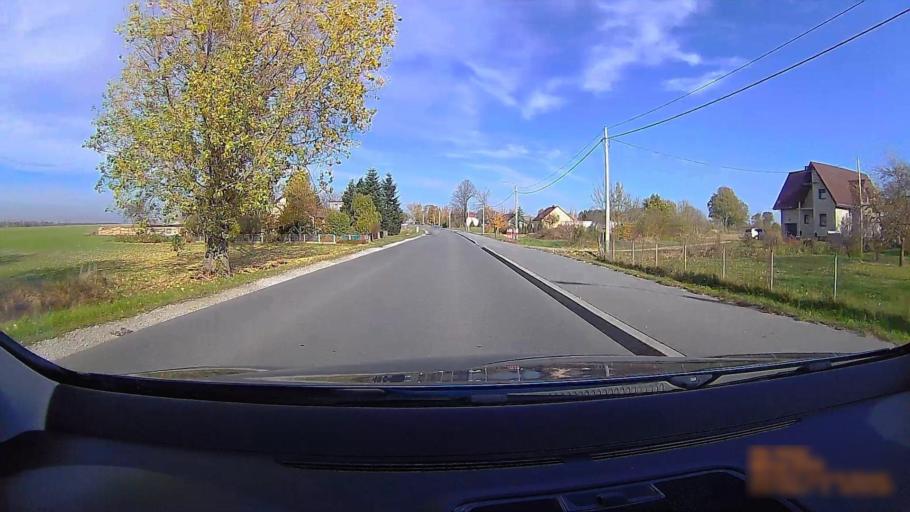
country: PL
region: Greater Poland Voivodeship
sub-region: Powiat kepinski
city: Kepno
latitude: 51.3301
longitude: 18.0176
